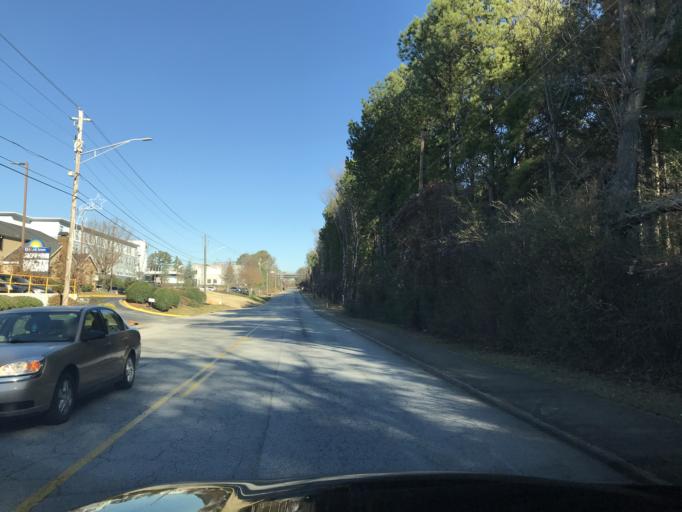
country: US
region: Georgia
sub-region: Fulton County
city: College Park
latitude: 33.6323
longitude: -84.4580
